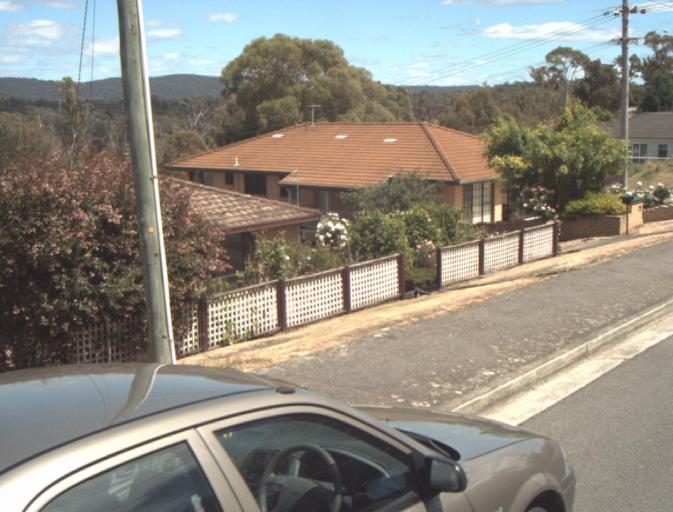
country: AU
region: Tasmania
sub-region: Launceston
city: West Launceston
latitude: -41.4558
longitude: 147.1238
